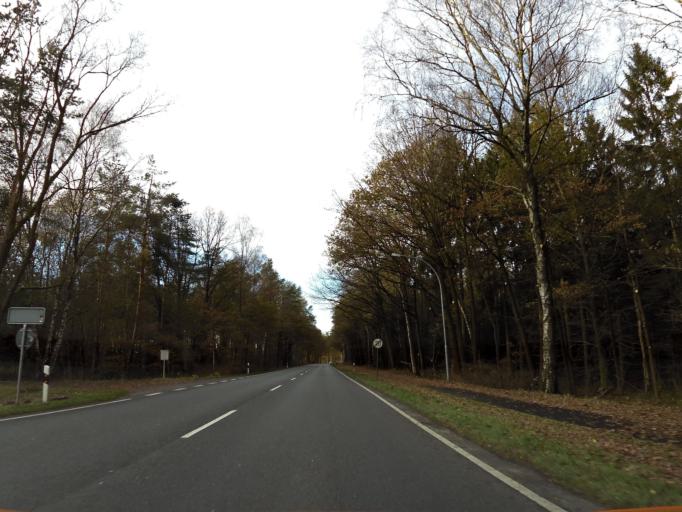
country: DE
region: Lower Saxony
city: Munster
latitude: 53.0110
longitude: 10.0262
